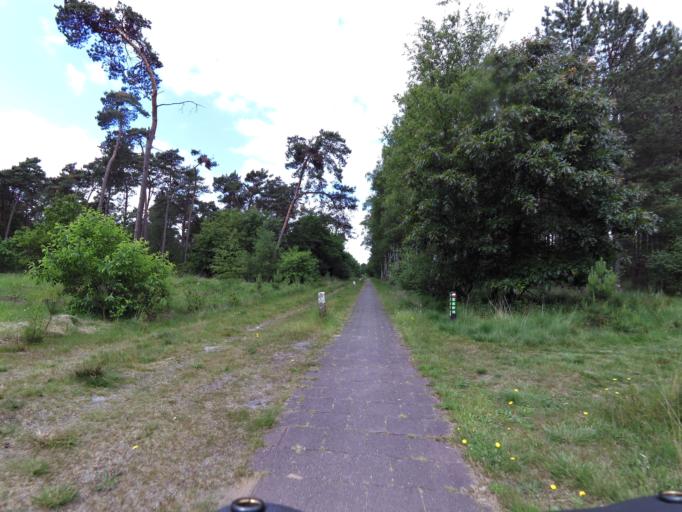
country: NL
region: North Brabant
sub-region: Gemeente Baarle-Nassau
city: Baarle-Nassau
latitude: 51.5018
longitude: 4.9184
